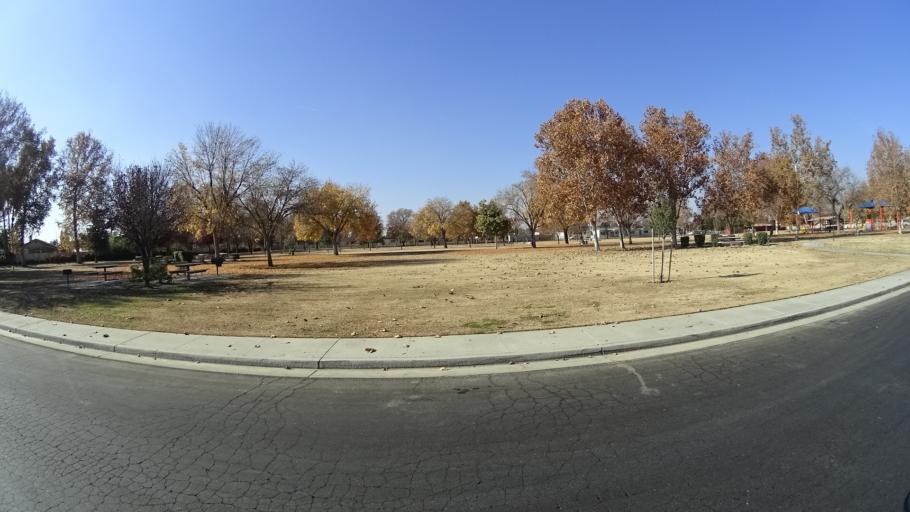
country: US
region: California
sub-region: Kern County
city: Greenfield
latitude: 35.3016
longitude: -119.0617
